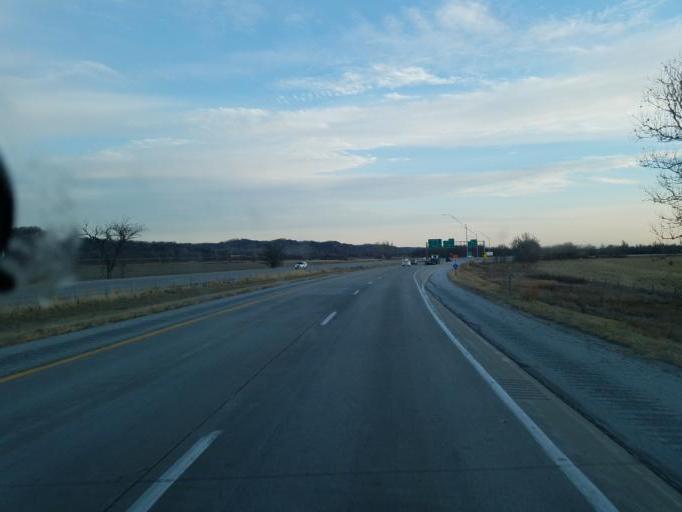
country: US
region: Iowa
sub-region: Harrison County
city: Missouri Valley
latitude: 41.5063
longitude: -95.9034
